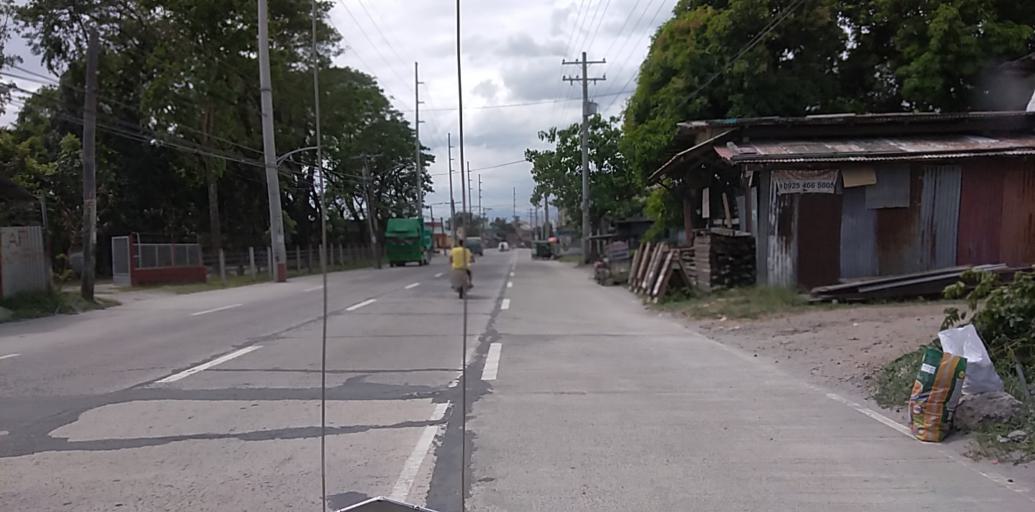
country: PH
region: Central Luzon
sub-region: Province of Pampanga
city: Pio
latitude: 15.0507
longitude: 120.5319
